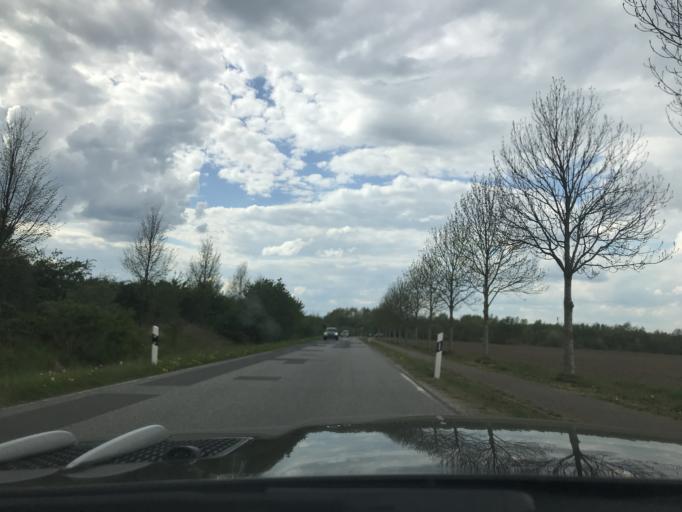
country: DE
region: Schleswig-Holstein
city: Gross Gronau
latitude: 53.7707
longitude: 10.7739
